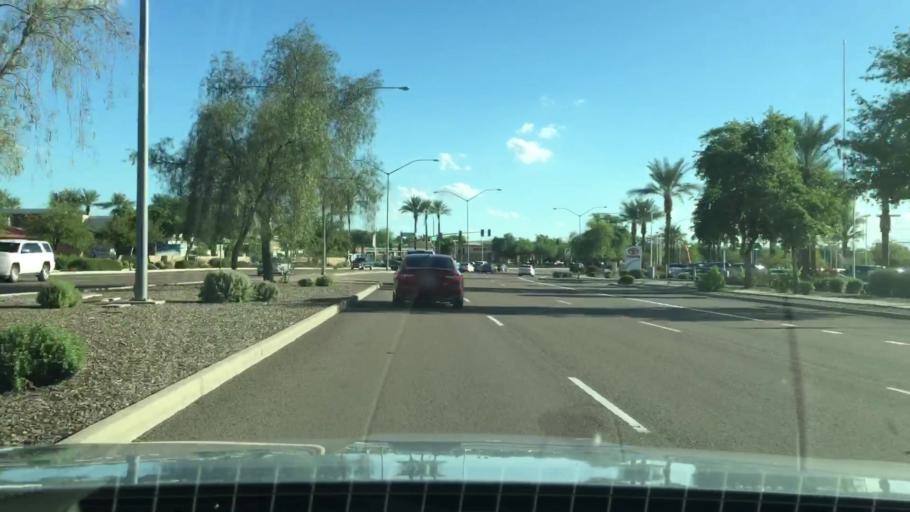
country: US
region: Arizona
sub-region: Maricopa County
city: Tempe
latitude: 33.4361
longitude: -111.8696
